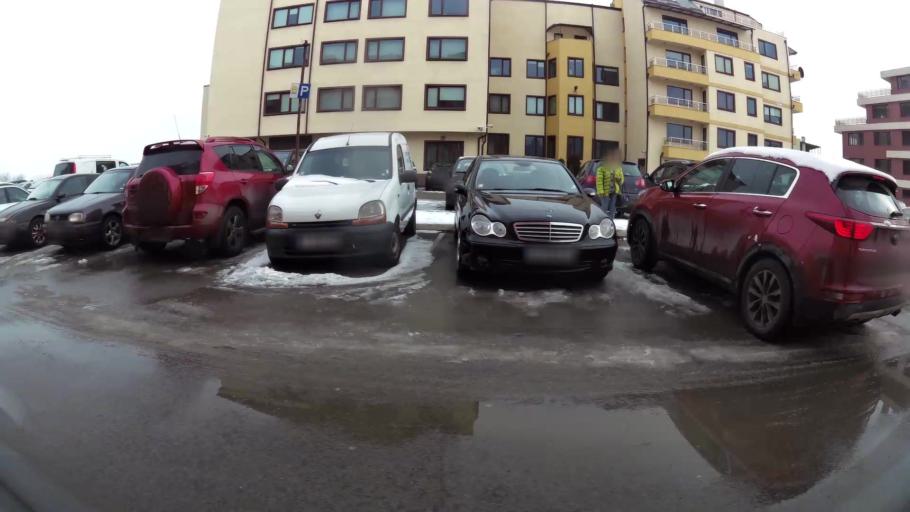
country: BG
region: Sofia-Capital
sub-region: Stolichna Obshtina
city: Sofia
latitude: 42.7155
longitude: 23.3795
